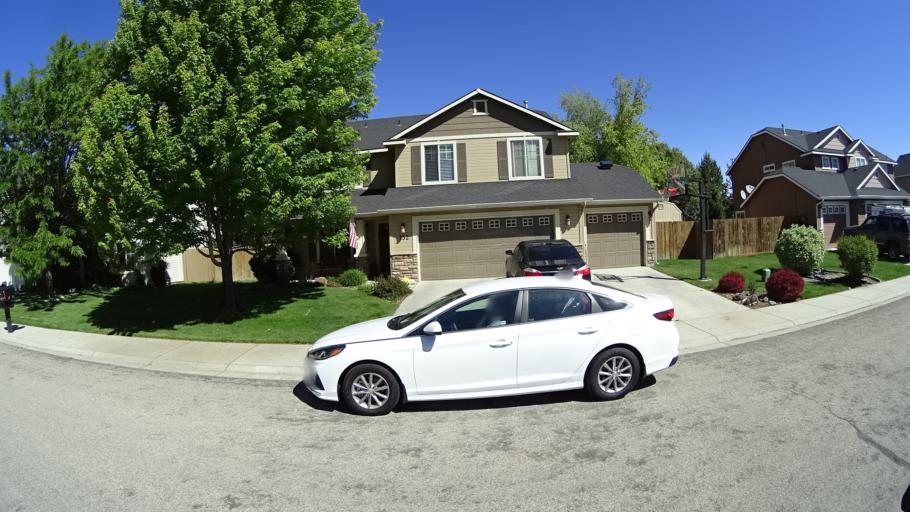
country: US
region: Idaho
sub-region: Ada County
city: Meridian
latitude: 43.6358
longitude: -116.3917
